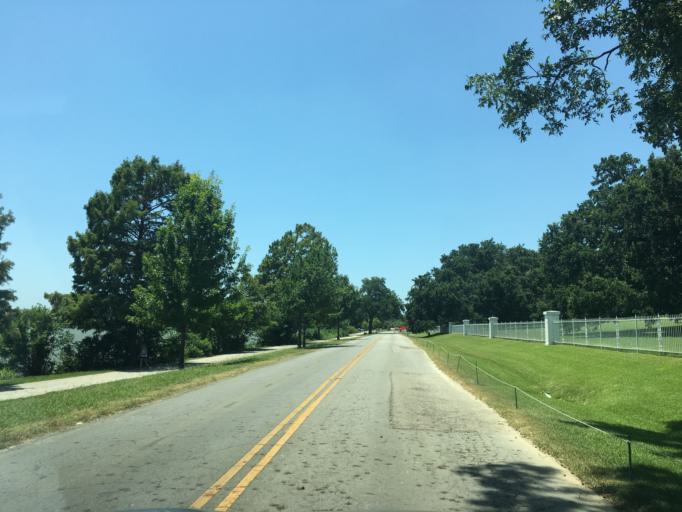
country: US
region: Texas
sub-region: Dallas County
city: Highland Park
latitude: 32.8353
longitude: -96.7255
